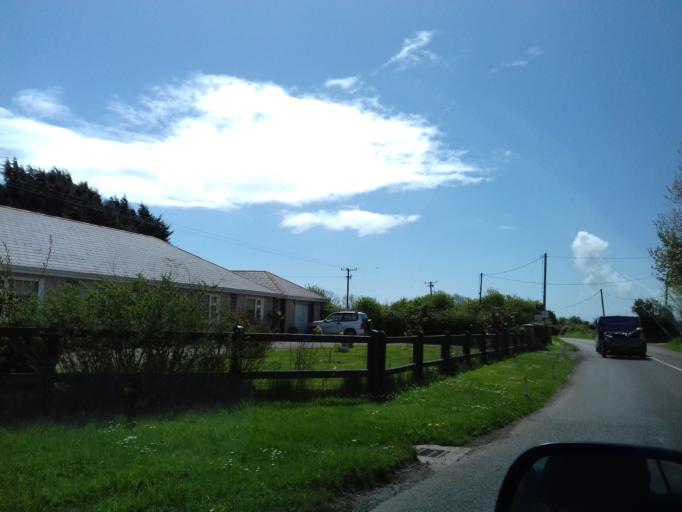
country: IE
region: Munster
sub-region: Waterford
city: Dunmore East
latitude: 52.2464
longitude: -6.8617
